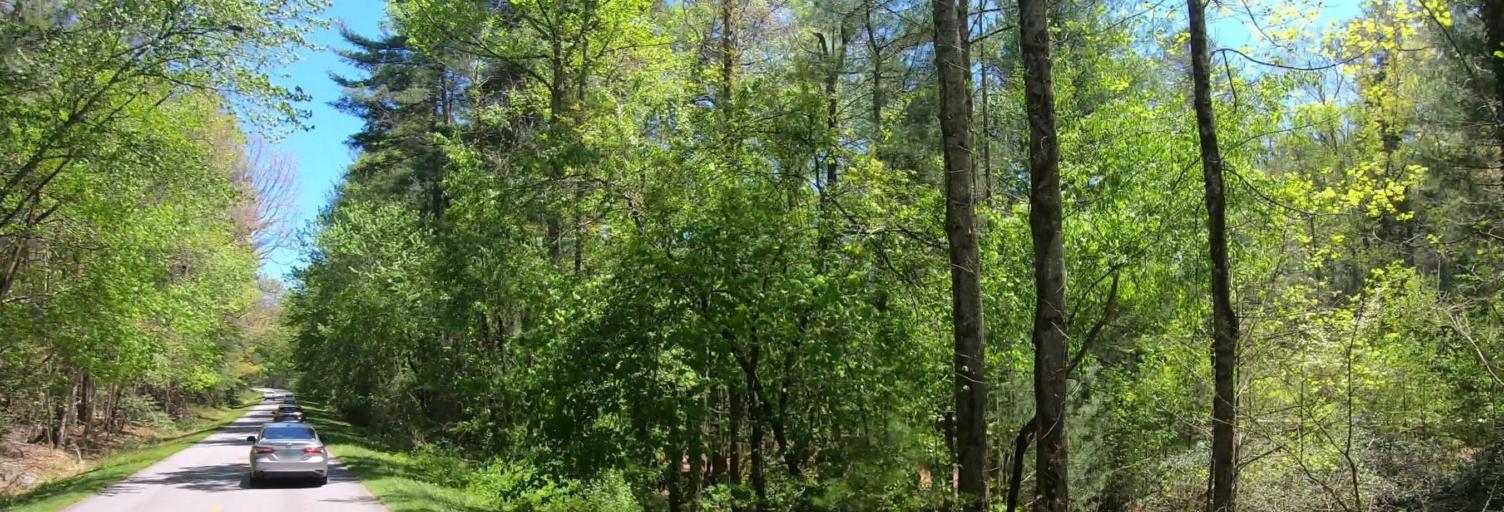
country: US
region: North Carolina
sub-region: Buncombe County
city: Biltmore Forest
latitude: 35.5169
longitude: -82.5364
